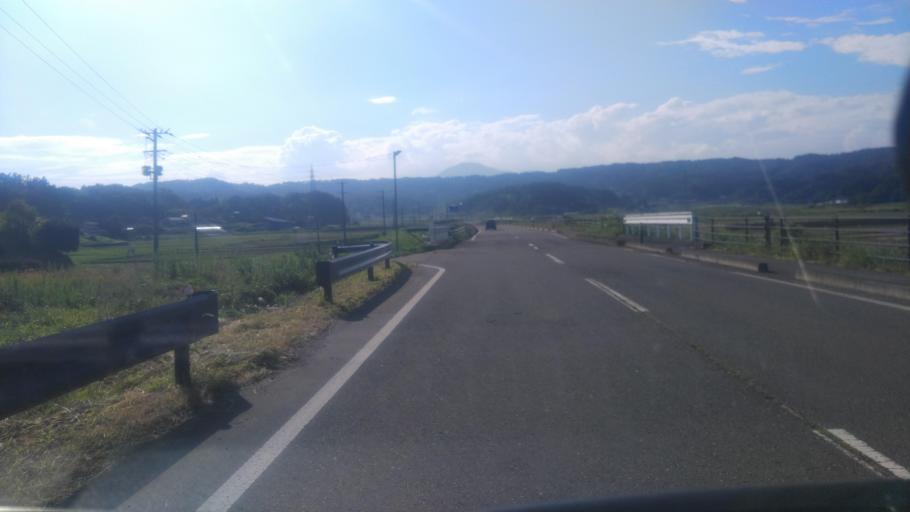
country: JP
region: Miyagi
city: Okawara
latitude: 38.0829
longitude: 140.7232
